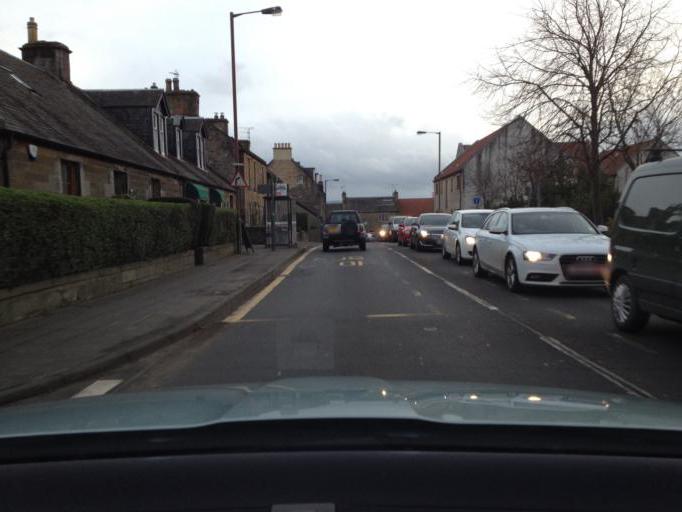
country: GB
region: Scotland
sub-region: Edinburgh
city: Kirkliston
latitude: 55.9553
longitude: -3.4014
